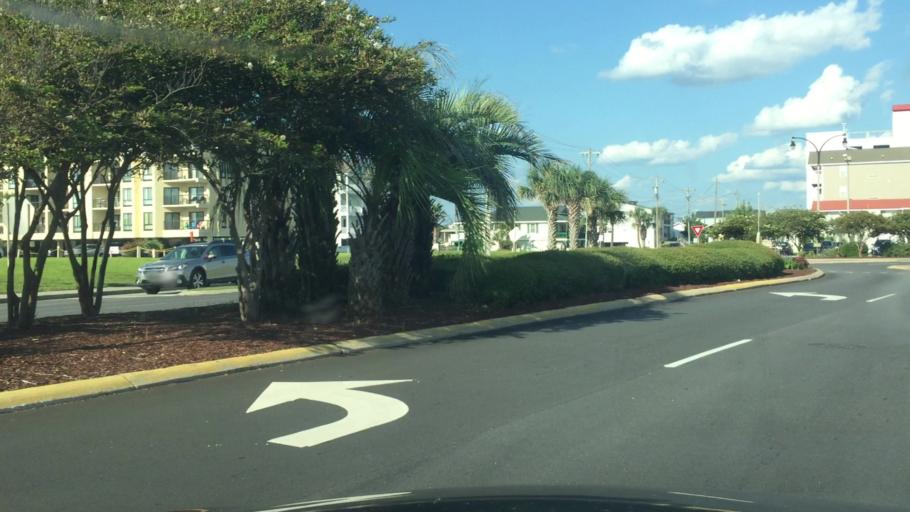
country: US
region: South Carolina
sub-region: Horry County
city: North Myrtle Beach
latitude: 33.8268
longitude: -78.6481
